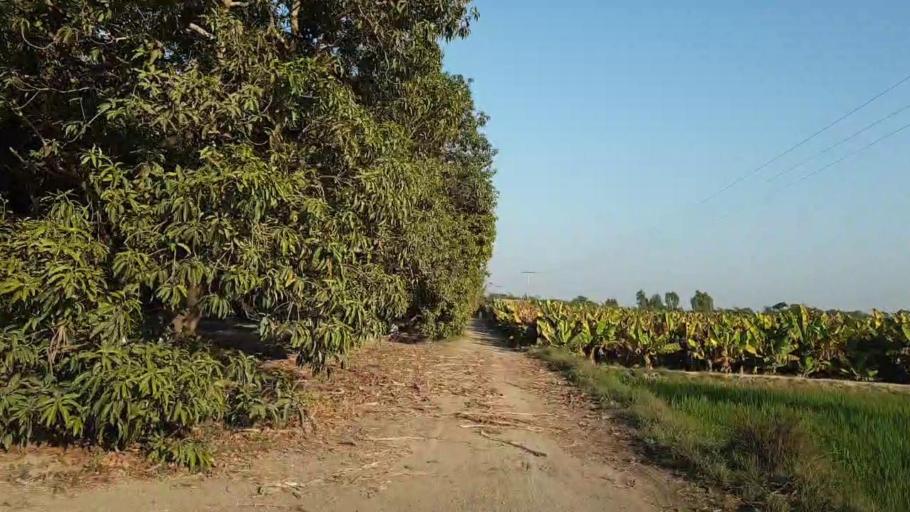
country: PK
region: Sindh
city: Tando Jam
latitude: 25.5037
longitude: 68.5566
